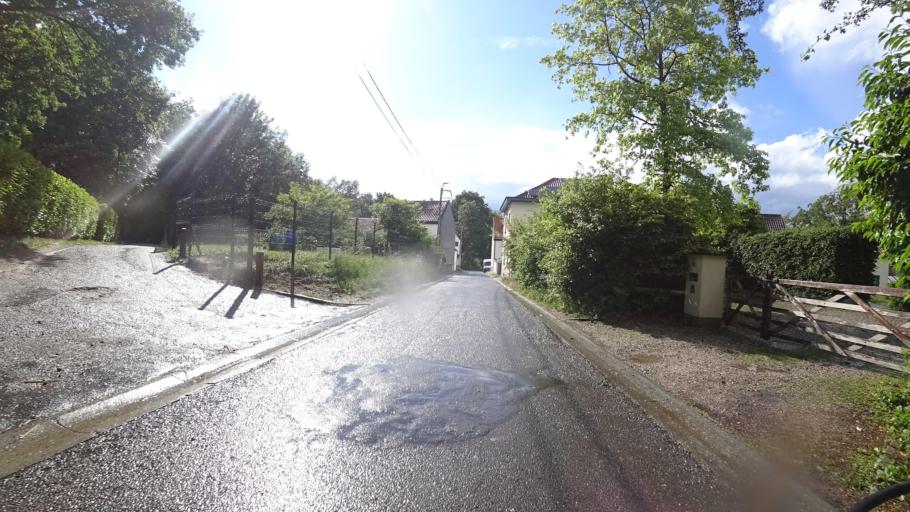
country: BE
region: Wallonia
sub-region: Province du Brabant Wallon
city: Wavre
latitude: 50.6914
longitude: 4.5923
